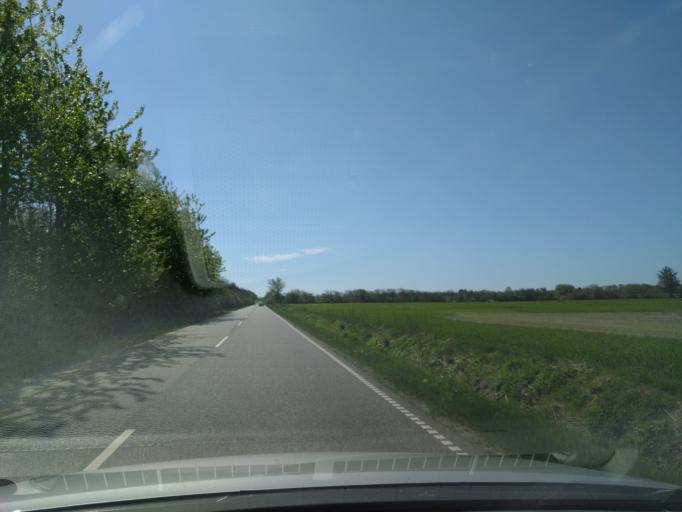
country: DK
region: Central Jutland
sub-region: Ringkobing-Skjern Kommune
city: Tarm
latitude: 55.8797
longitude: 8.5270
